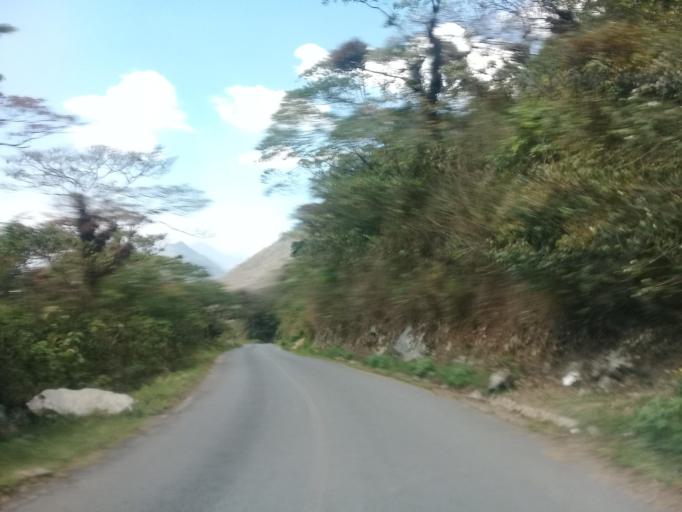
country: MX
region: Veracruz
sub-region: Tlilapan
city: Tonalixco
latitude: 18.8131
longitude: -97.0588
